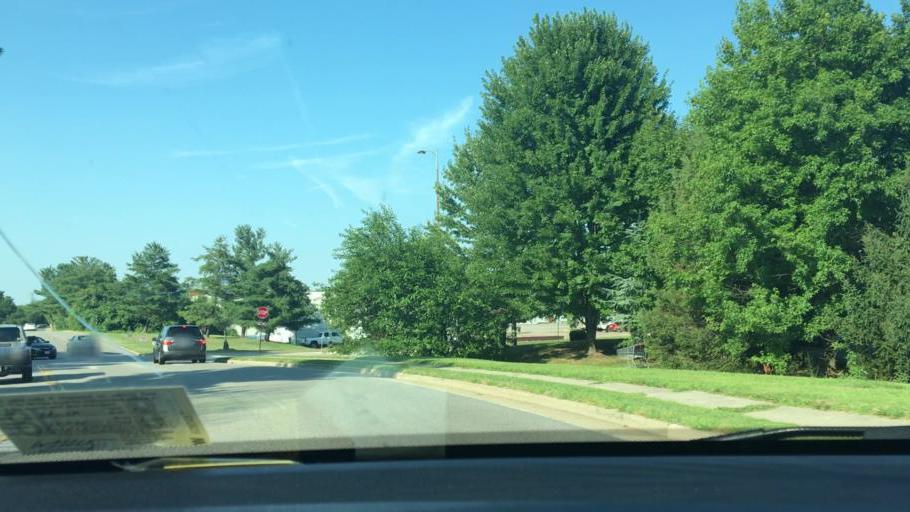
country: US
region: Virginia
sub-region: Prince William County
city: Potomac Mills
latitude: 38.6407
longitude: -77.2919
